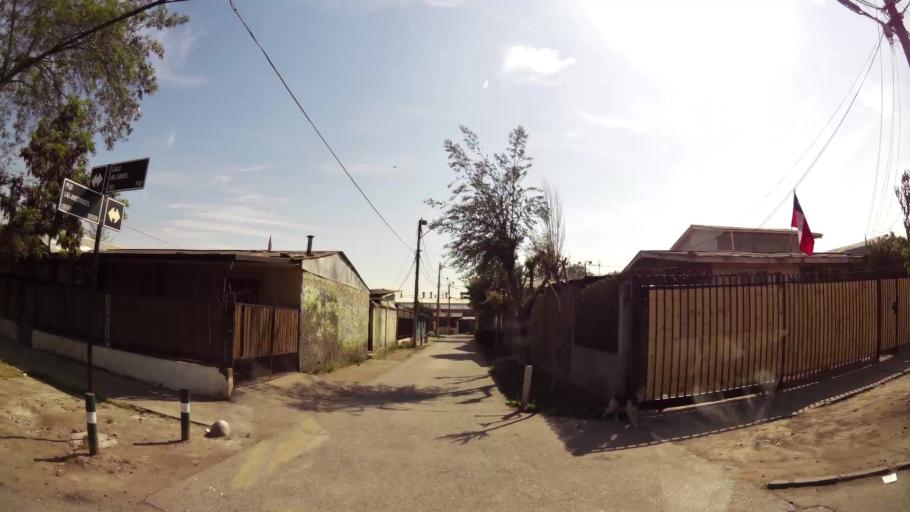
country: CL
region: Santiago Metropolitan
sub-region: Provincia de Santiago
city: La Pintana
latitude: -33.5598
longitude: -70.6652
